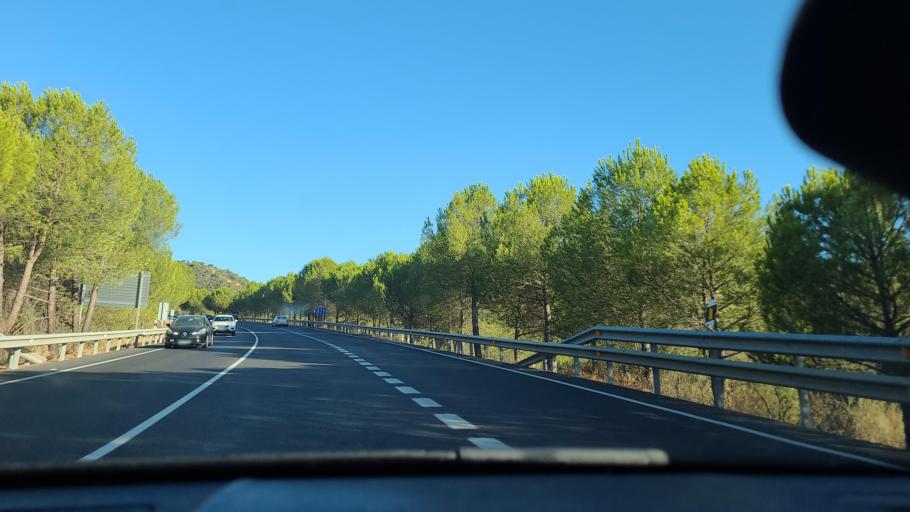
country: ES
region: Andalusia
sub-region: Province of Cordoba
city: Villaharta
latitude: 38.1217
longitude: -4.8966
